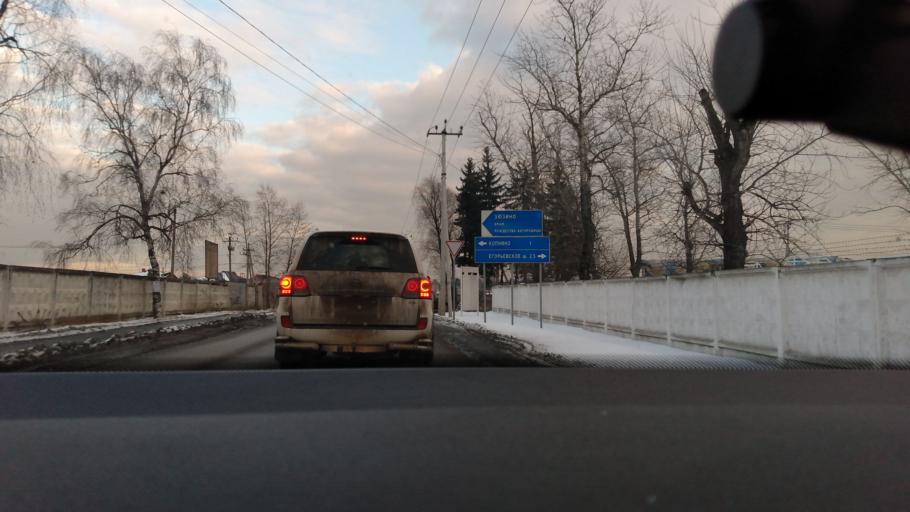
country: RU
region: Moskovskaya
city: Rodniki
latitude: 55.6784
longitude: 38.1098
